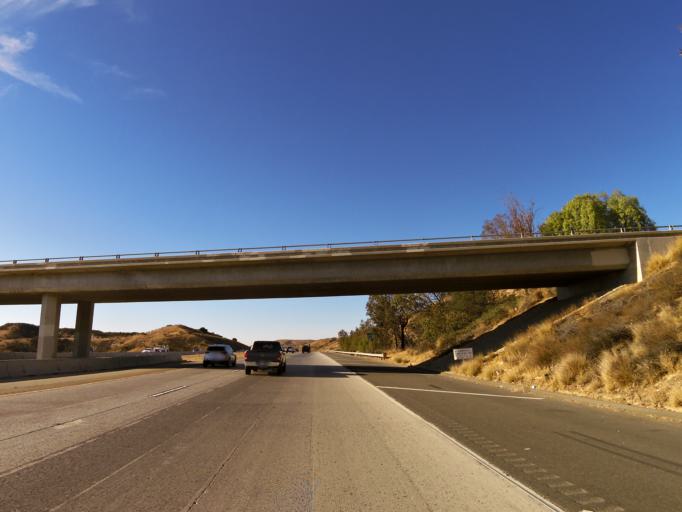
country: US
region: California
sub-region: Ventura County
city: Simi Valley
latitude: 34.2872
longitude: -118.7988
